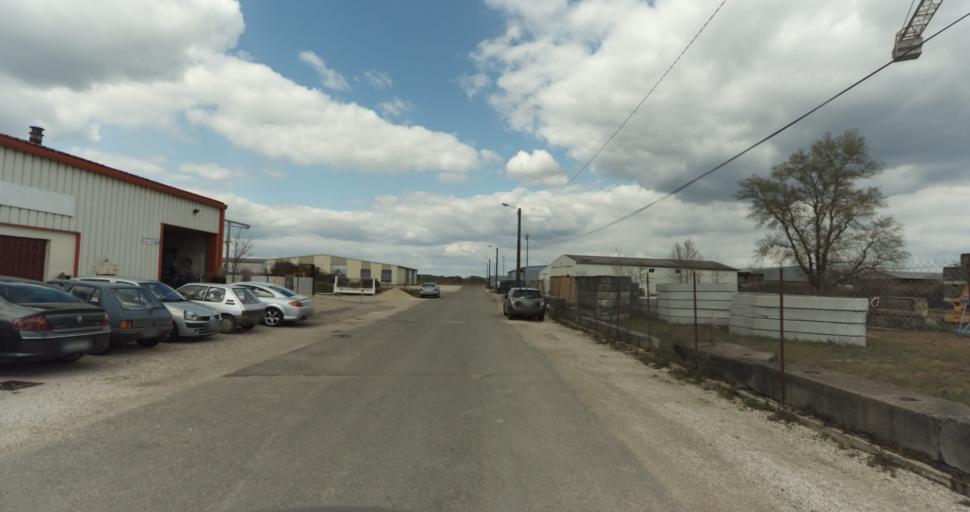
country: FR
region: Bourgogne
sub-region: Departement de la Cote-d'Or
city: Auxonne
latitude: 47.1944
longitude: 5.4165
